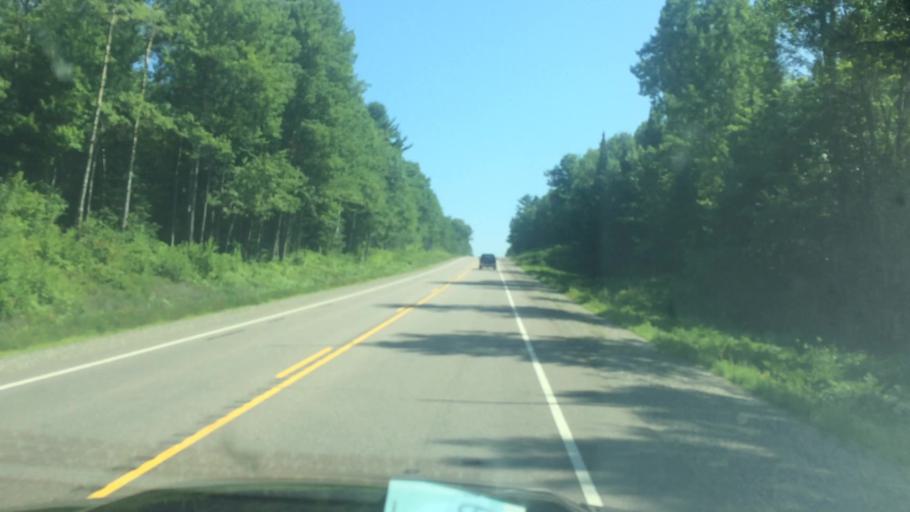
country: US
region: Wisconsin
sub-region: Lincoln County
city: Tomahawk
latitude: 45.5495
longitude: -89.6596
